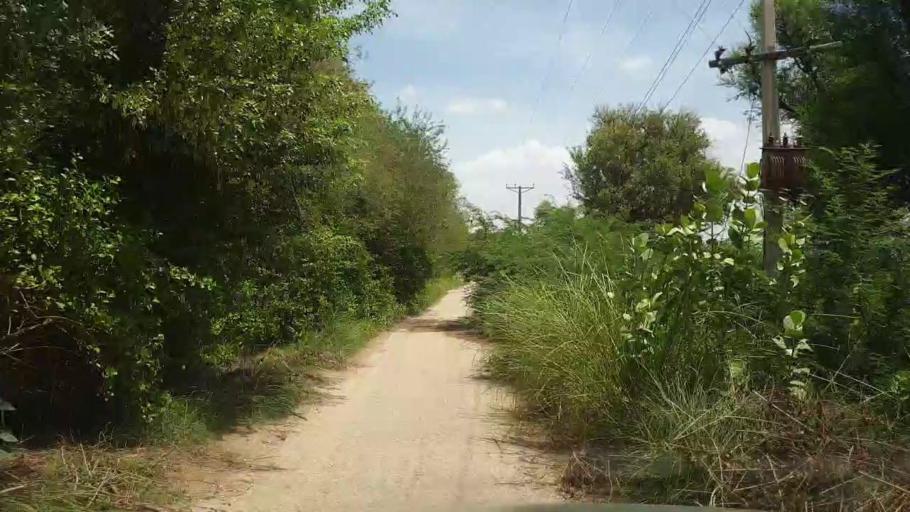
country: PK
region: Sindh
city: Kot Diji
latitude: 27.1357
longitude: 69.0075
